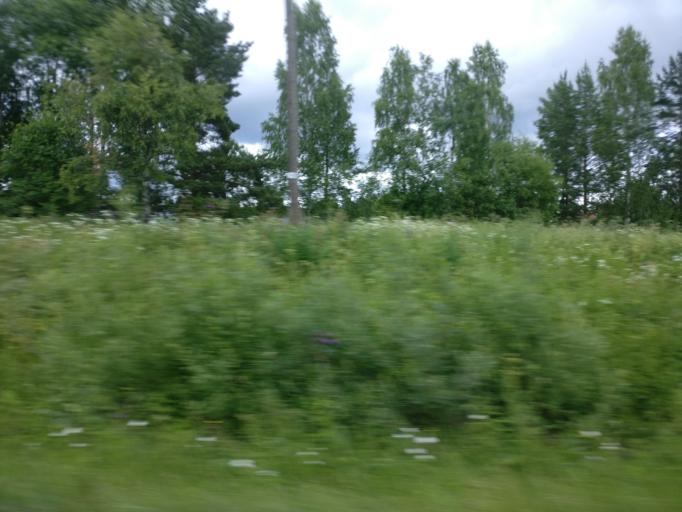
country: FI
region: Northern Savo
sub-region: Varkaus
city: Kangaslampi
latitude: 62.1599
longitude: 28.1519
